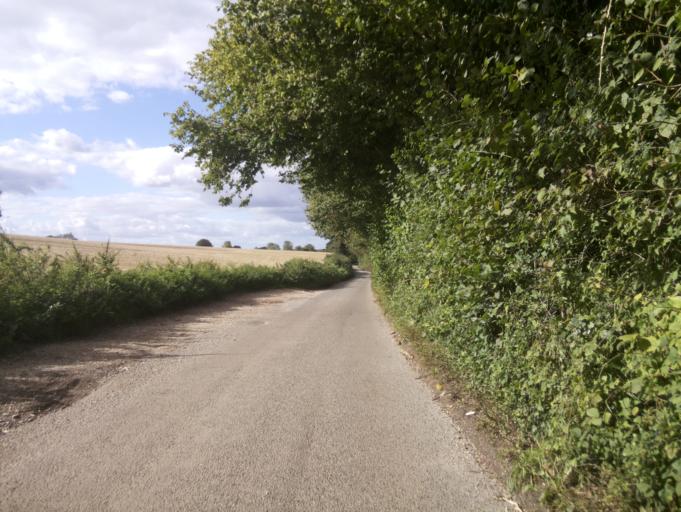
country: GB
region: England
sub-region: Hampshire
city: Chandlers Ford
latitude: 51.0680
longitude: -1.3798
